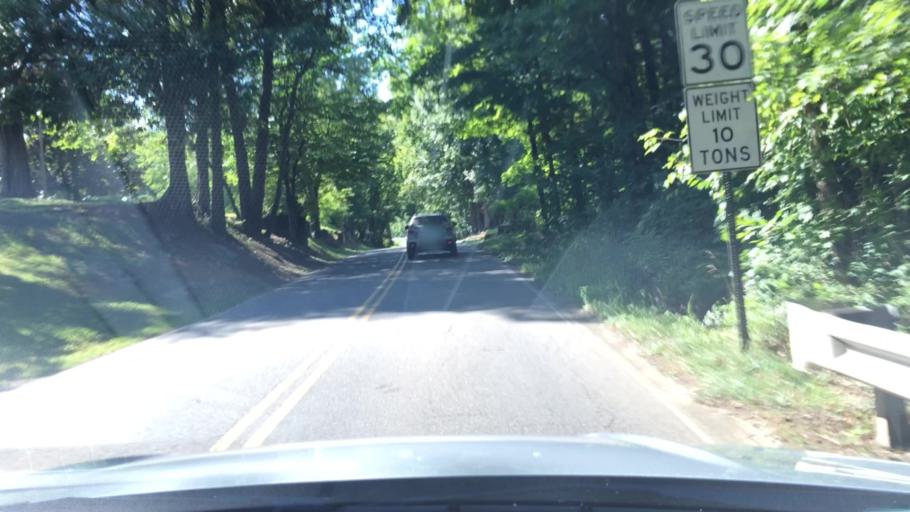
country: US
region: Tennessee
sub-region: Loudon County
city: Greenback
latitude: 35.7561
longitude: -84.1327
